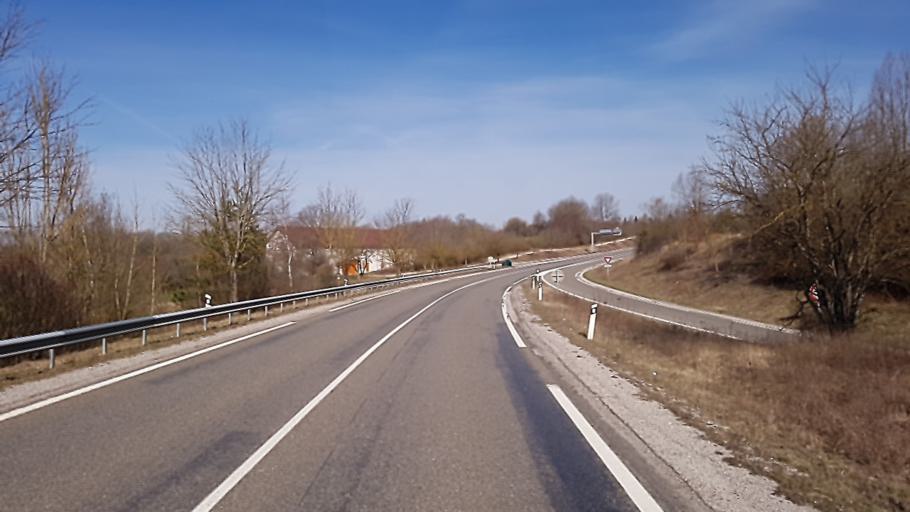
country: FR
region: Franche-Comte
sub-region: Departement du Jura
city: Champagnole
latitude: 46.7611
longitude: 5.9064
